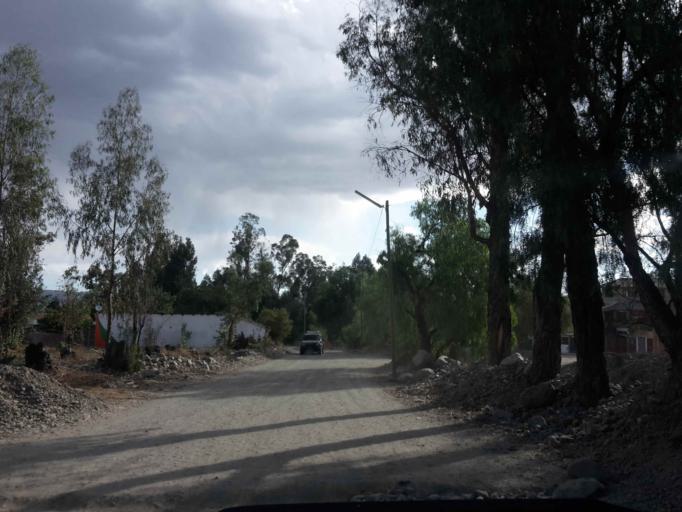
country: BO
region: Cochabamba
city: Cochabamba
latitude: -17.3491
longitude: -66.2005
